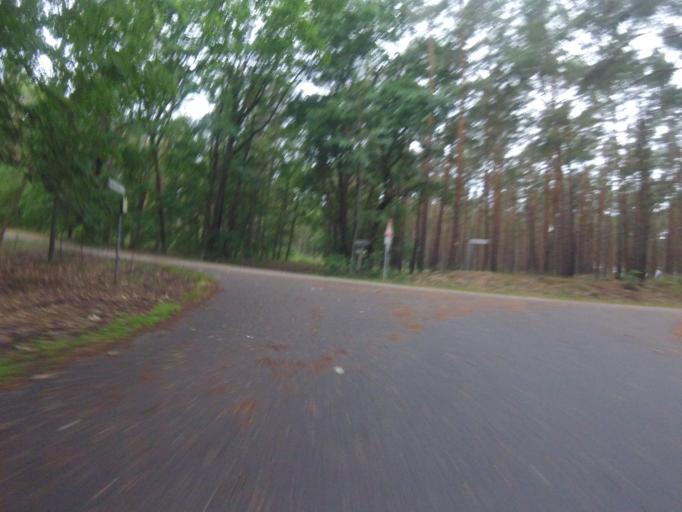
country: DE
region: Brandenburg
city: Bestensee
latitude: 52.2246
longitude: 13.7071
